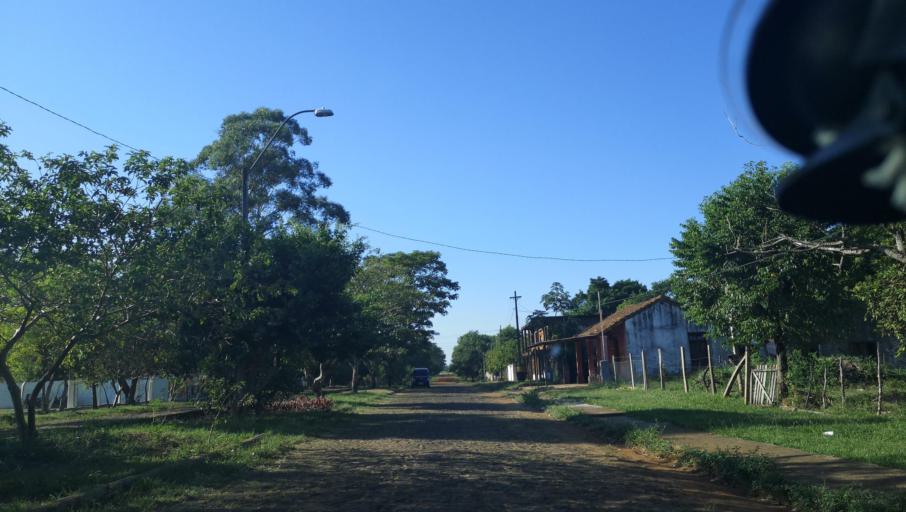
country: PY
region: Itapua
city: Carmen del Parana
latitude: -27.1681
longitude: -56.2416
